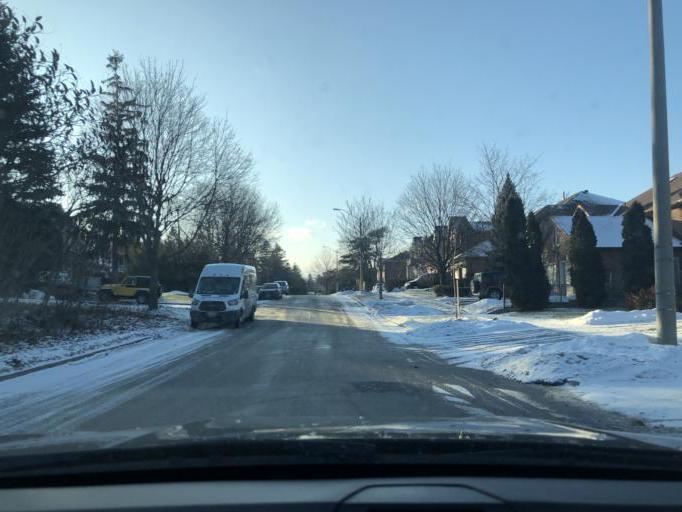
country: CA
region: Ontario
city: Scarborough
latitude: 43.7796
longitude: -79.1525
